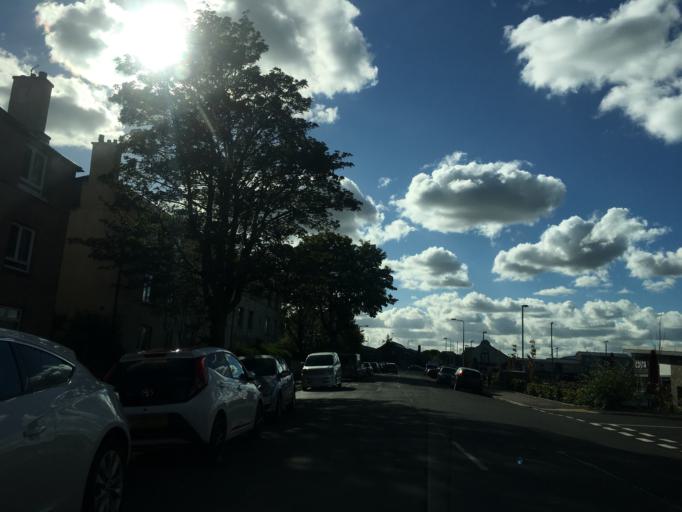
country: GB
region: Scotland
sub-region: Edinburgh
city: Colinton
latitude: 55.9296
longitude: -3.2448
